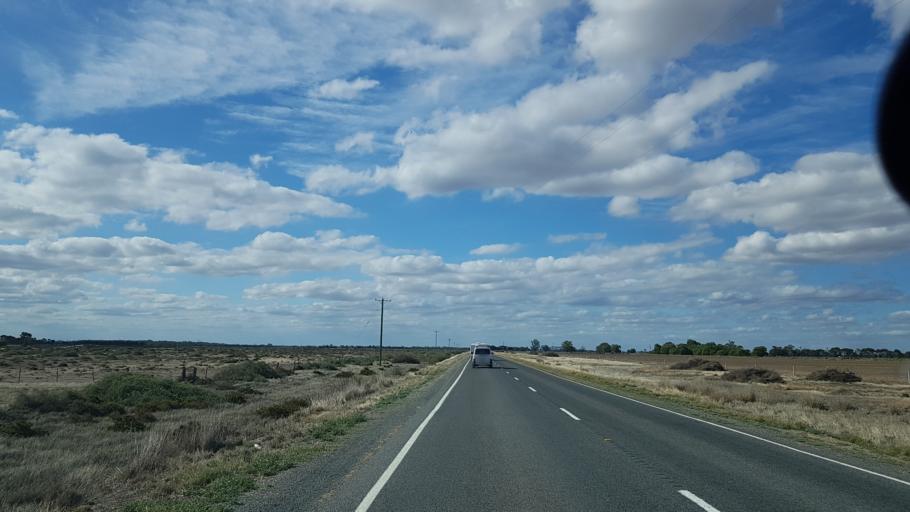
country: AU
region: Victoria
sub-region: Swan Hill
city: Swan Hill
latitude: -35.8415
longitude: 143.9392
